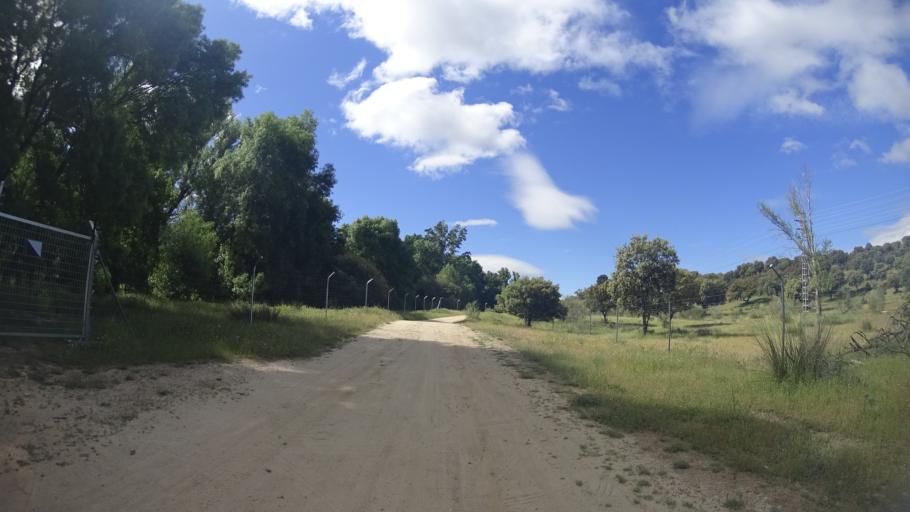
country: ES
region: Madrid
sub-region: Provincia de Madrid
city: Villanueva del Pardillo
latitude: 40.4362
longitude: -3.9523
